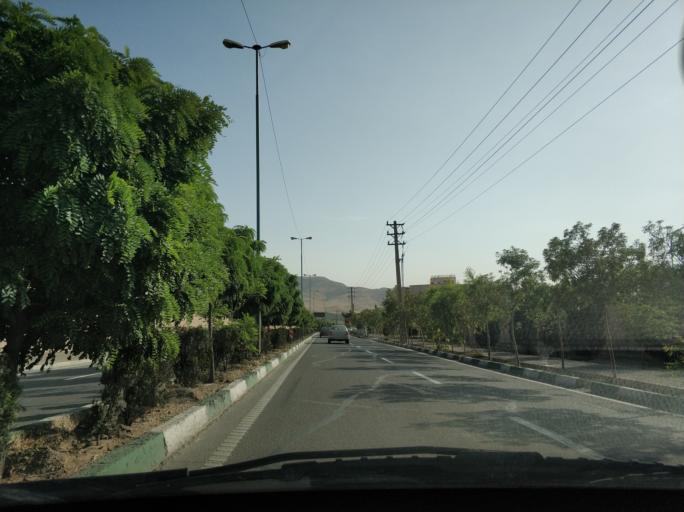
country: IR
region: Tehran
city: Tehran
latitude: 35.7299
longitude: 51.5930
